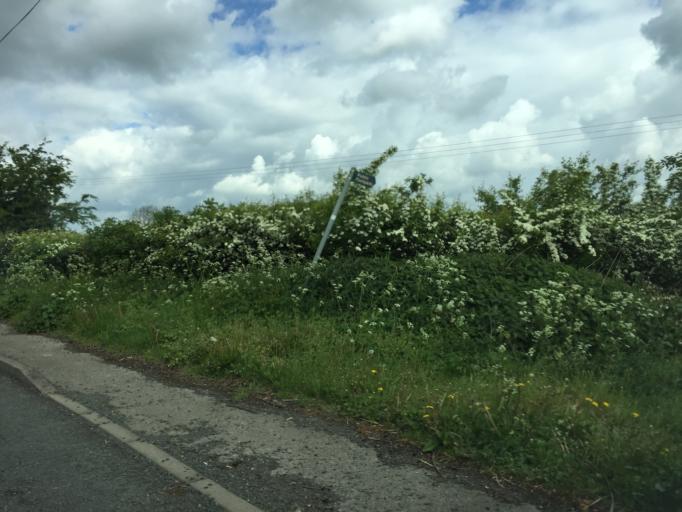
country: GB
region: England
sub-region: Gloucestershire
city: Stonehouse
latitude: 51.7725
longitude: -2.2847
